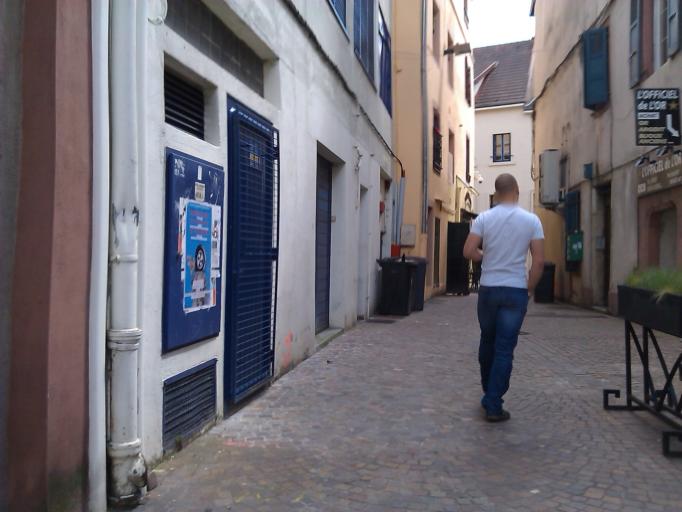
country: FR
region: Franche-Comte
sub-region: Departement du Doubs
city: Montbeliard
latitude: 47.5098
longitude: 6.7971
